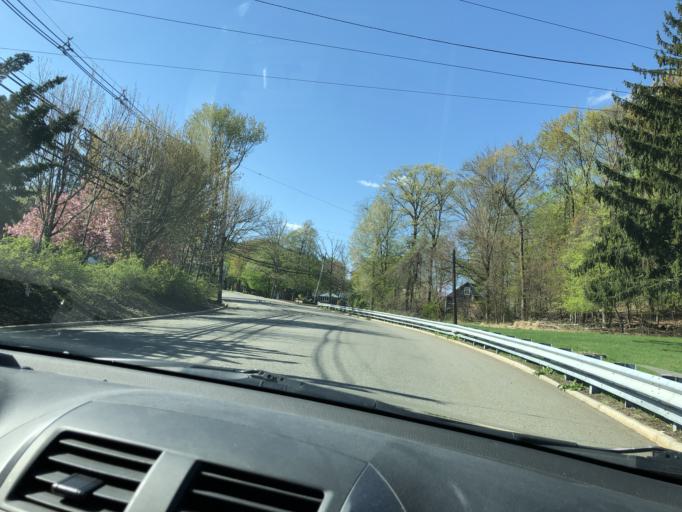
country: US
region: New Jersey
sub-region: Essex County
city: North Caldwell
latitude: 40.8585
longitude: -74.2591
